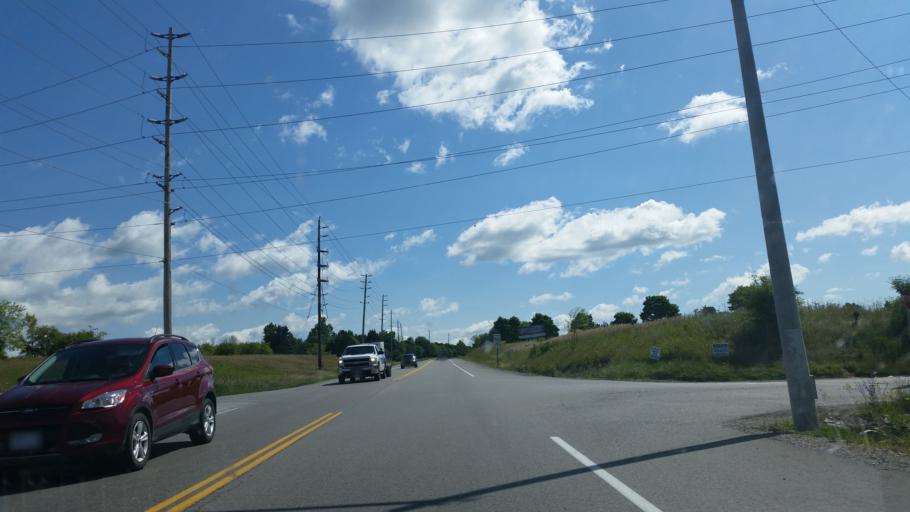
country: CA
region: Ontario
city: Vaughan
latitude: 43.8962
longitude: -79.6768
